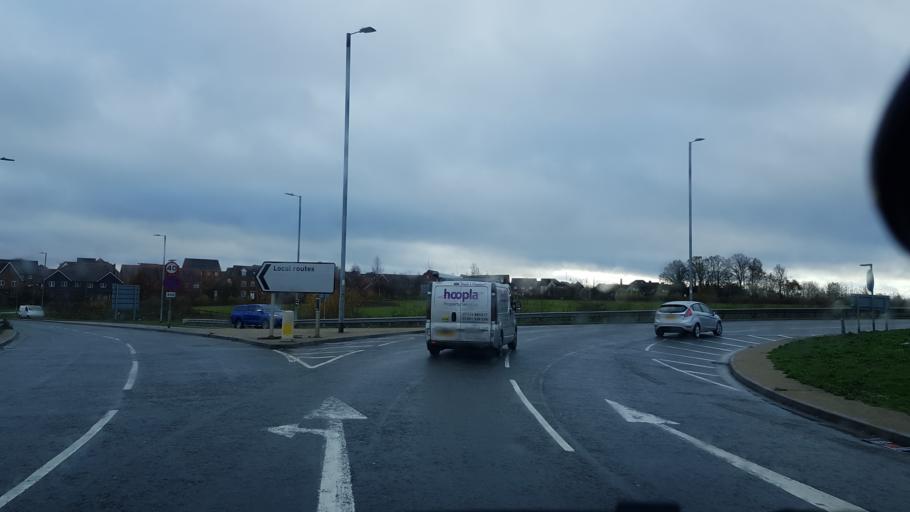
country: GB
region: England
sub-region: Bracknell Forest
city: Binfield
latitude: 51.4098
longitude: -0.7870
